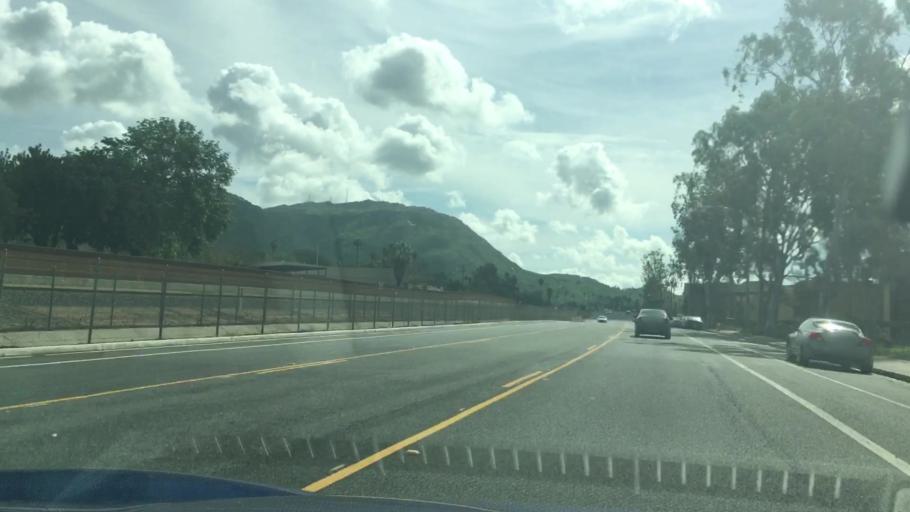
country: US
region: California
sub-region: Riverside County
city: Highgrove
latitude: 33.9860
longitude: -117.3294
